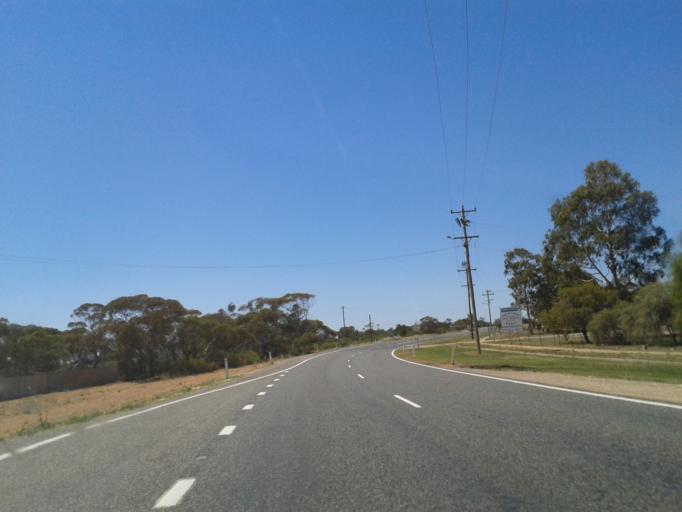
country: AU
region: New South Wales
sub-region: Wentworth
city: Dareton
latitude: -34.0939
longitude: 142.0565
